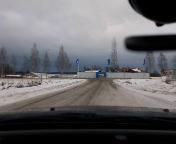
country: SE
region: Gaevleborg
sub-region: Bollnas Kommun
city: Bollnas
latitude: 61.3400
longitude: 16.3861
